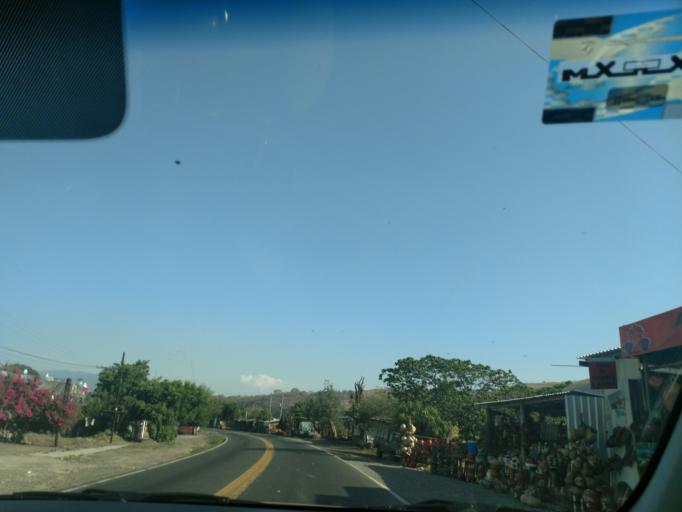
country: MX
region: Nayarit
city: San Pedro Lagunillas
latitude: 21.1587
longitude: -104.6257
